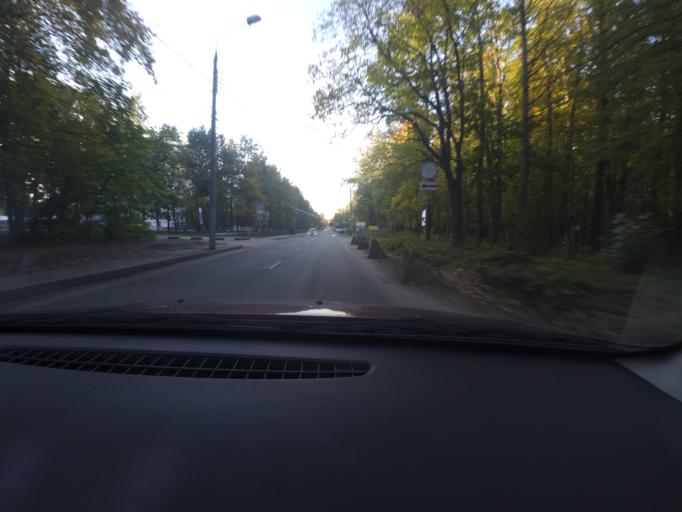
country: RU
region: Nizjnij Novgorod
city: Nizhniy Novgorod
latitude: 56.2693
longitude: 43.9948
